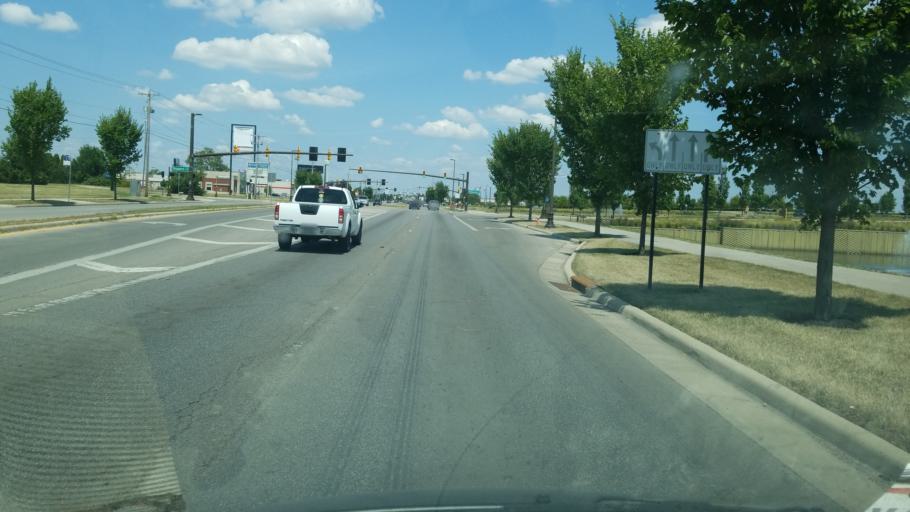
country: US
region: Ohio
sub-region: Franklin County
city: Lincoln Village
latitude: 39.9481
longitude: -83.1108
